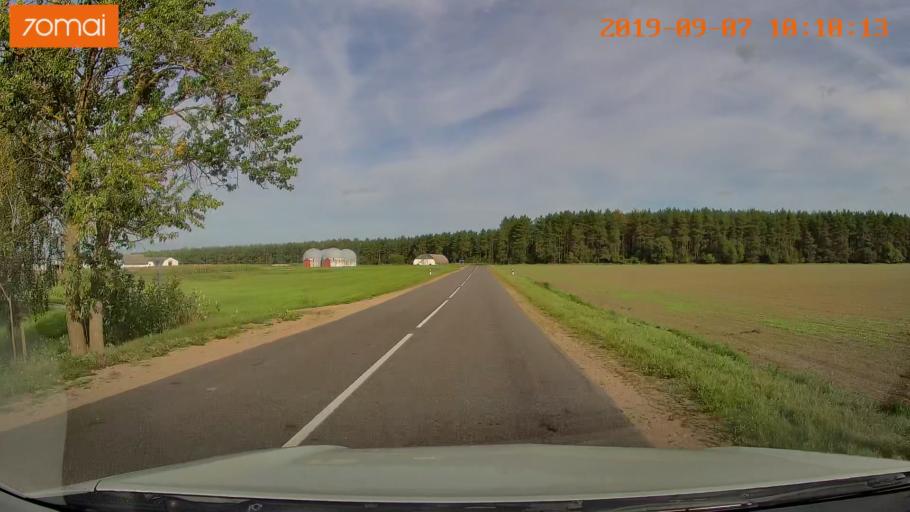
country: BY
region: Grodnenskaya
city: Voranava
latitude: 54.1058
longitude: 25.3713
